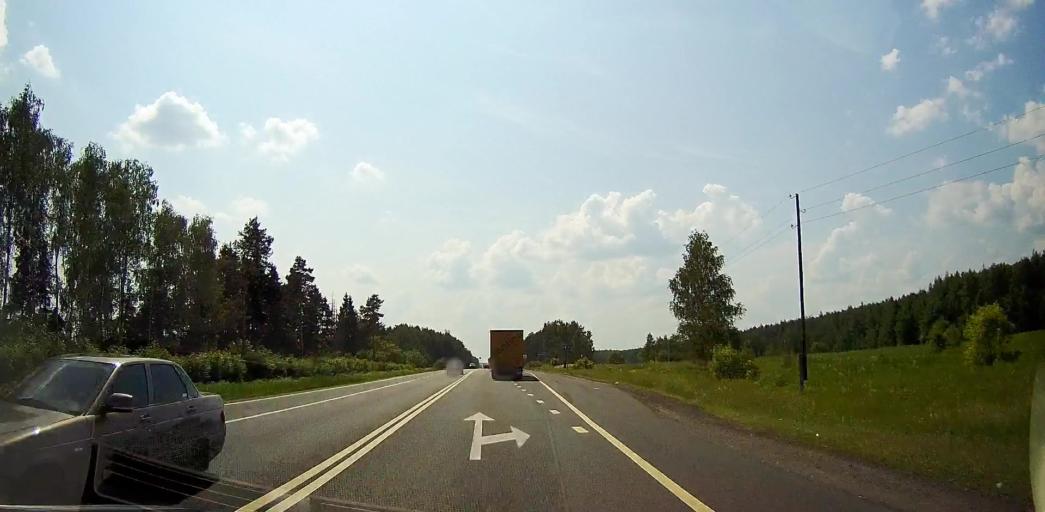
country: RU
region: Moskovskaya
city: Meshcherino
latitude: 55.1745
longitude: 38.3337
